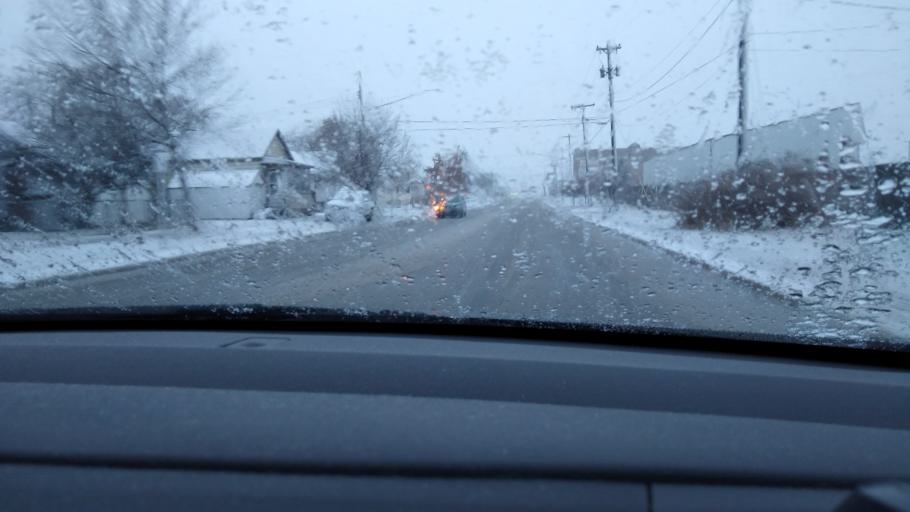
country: US
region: Michigan
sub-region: Delta County
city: Escanaba
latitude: 45.7494
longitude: -87.0672
